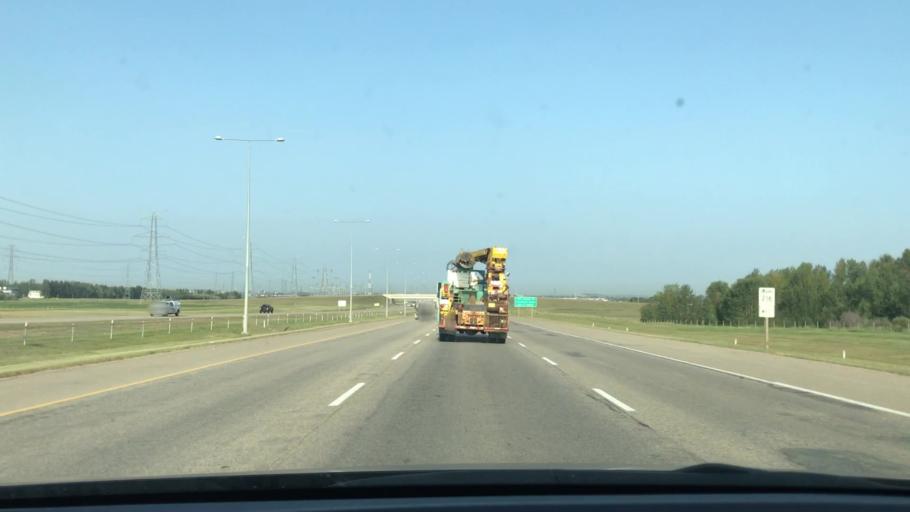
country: CA
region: Alberta
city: Beaumont
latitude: 53.4358
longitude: -113.4302
